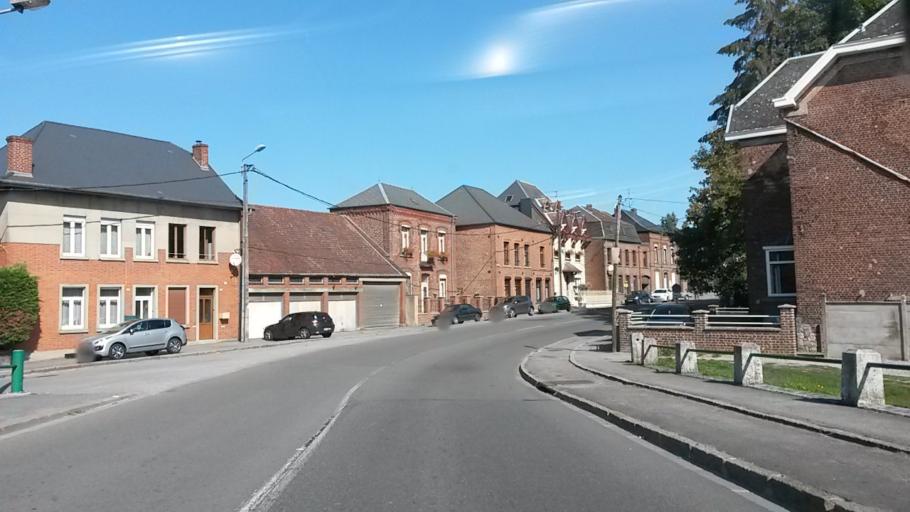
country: FR
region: Nord-Pas-de-Calais
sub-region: Departement du Nord
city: Avesnes-sur-Helpe
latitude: 50.1260
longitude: 3.9359
